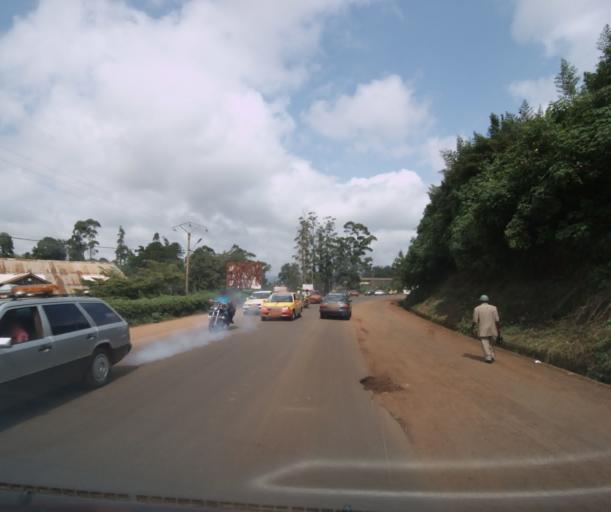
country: CM
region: West
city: Dschang
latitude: 5.4504
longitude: 10.0648
